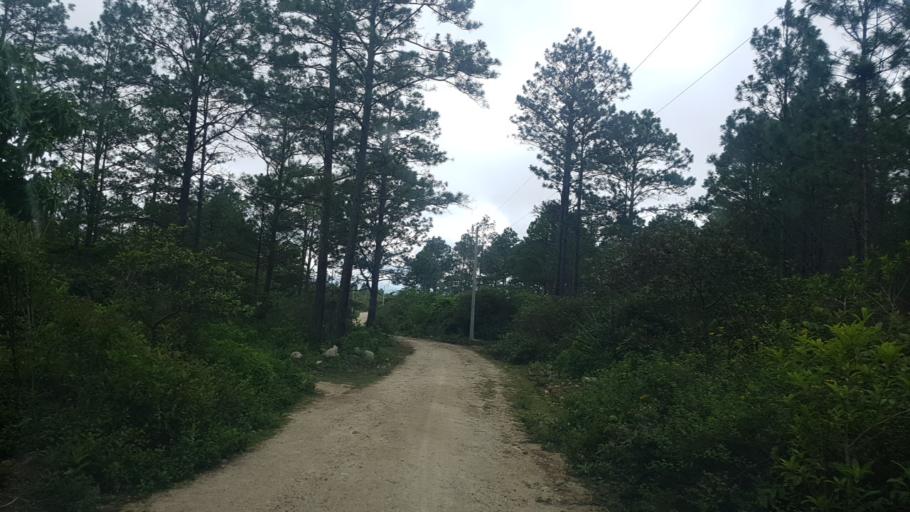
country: NI
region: Madriz
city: Totogalpa
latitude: 13.6140
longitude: -86.6085
